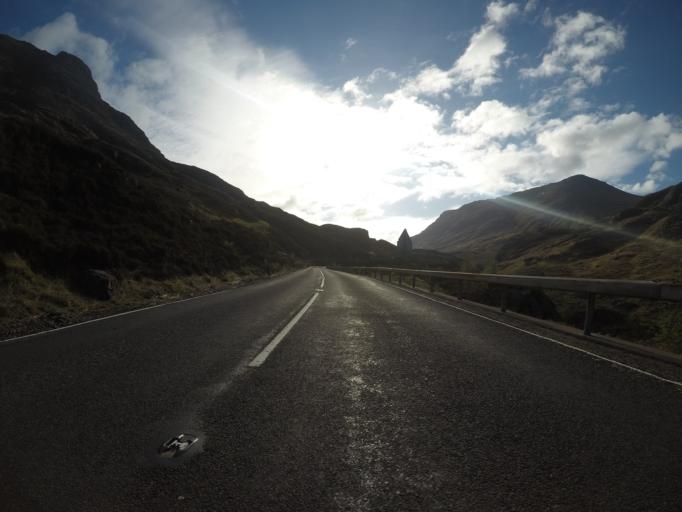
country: GB
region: Scotland
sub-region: Highland
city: Fort William
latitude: 56.6649
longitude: -4.9744
